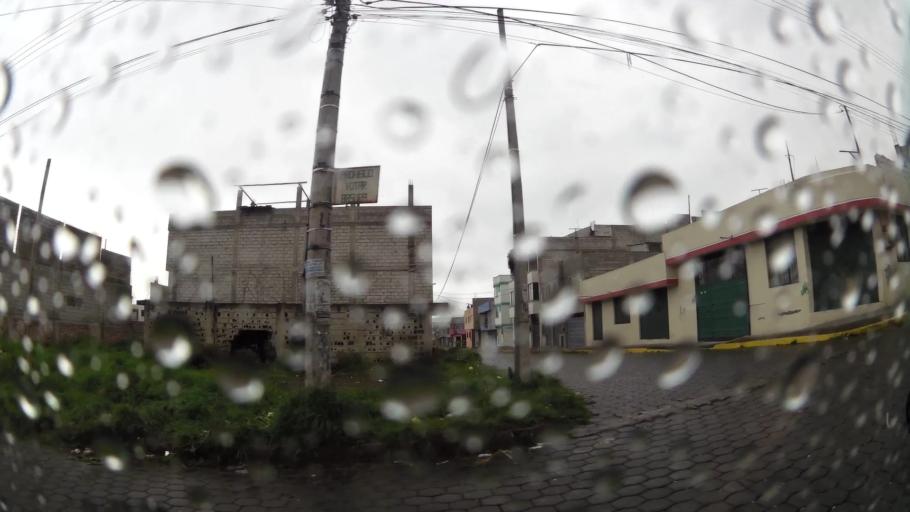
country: EC
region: Pichincha
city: Quito
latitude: -0.3218
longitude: -78.5549
